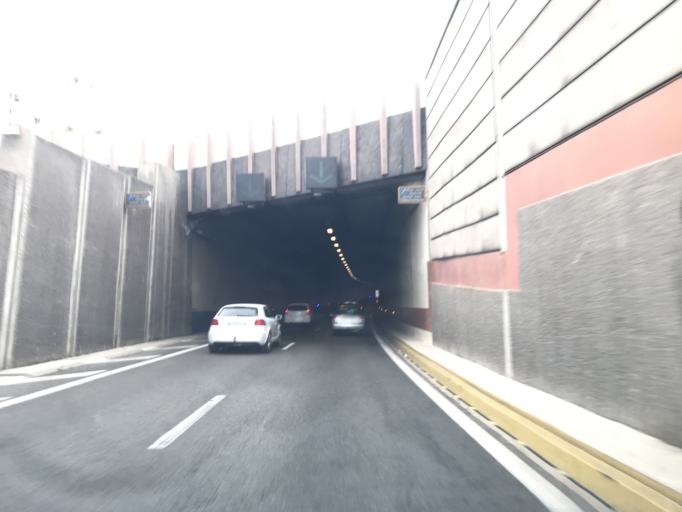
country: FR
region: Provence-Alpes-Cote d'Azur
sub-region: Departement du Var
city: Toulon
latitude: 43.1203
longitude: 5.9498
